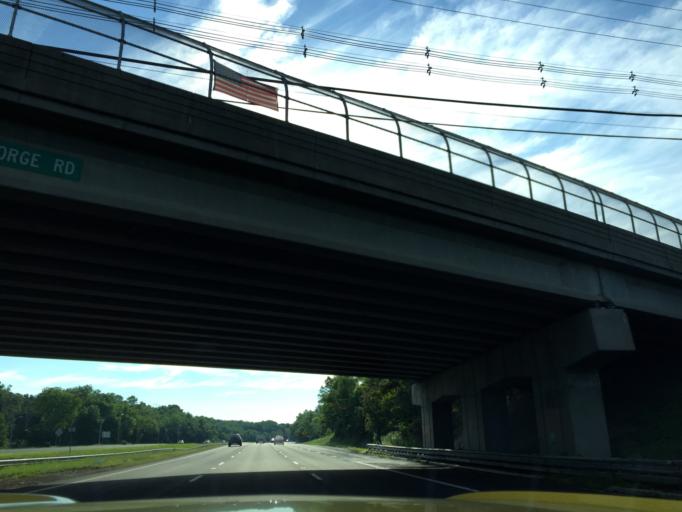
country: US
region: New Jersey
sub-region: Somerset County
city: Warren Township
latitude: 40.6476
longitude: -74.5229
